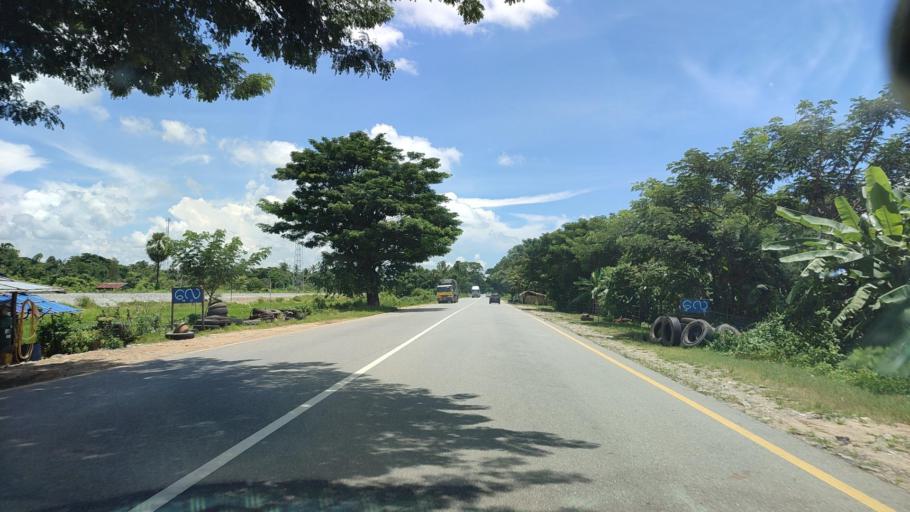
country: MM
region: Bago
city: Pyu
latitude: 18.3804
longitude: 96.4724
